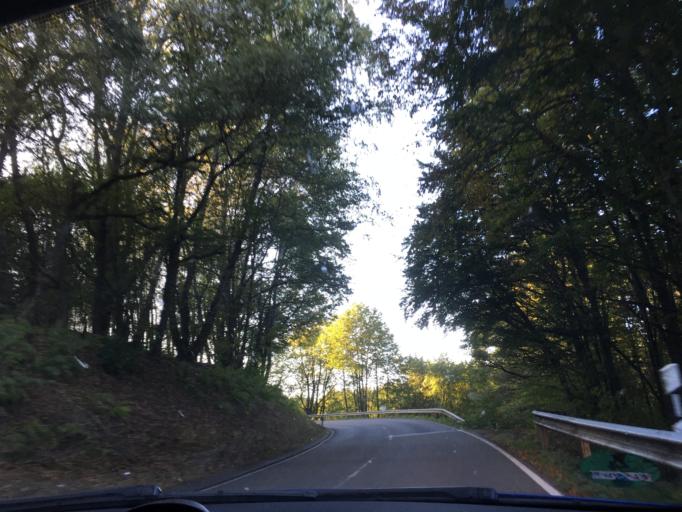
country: DE
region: Rheinland-Pfalz
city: Steinalben
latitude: 49.3223
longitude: 7.6444
